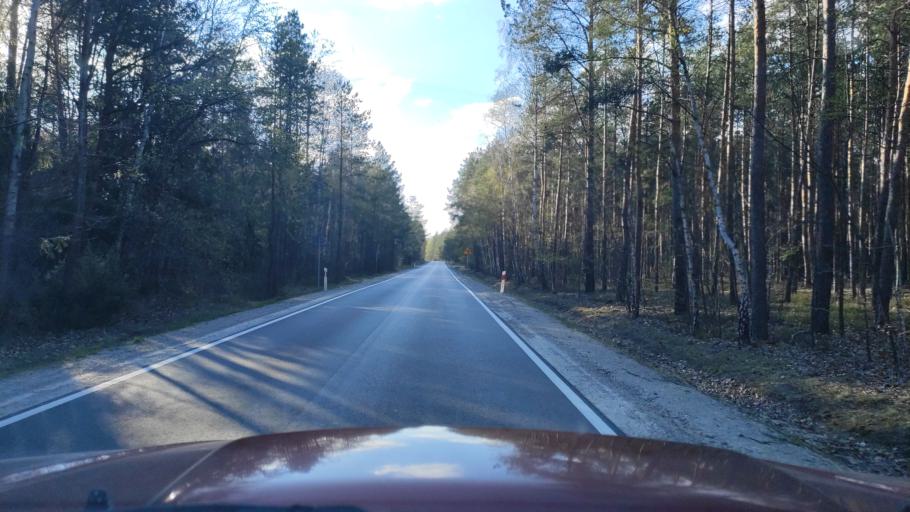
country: PL
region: Masovian Voivodeship
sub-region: Powiat zwolenski
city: Zwolen
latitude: 51.4049
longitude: 21.5309
